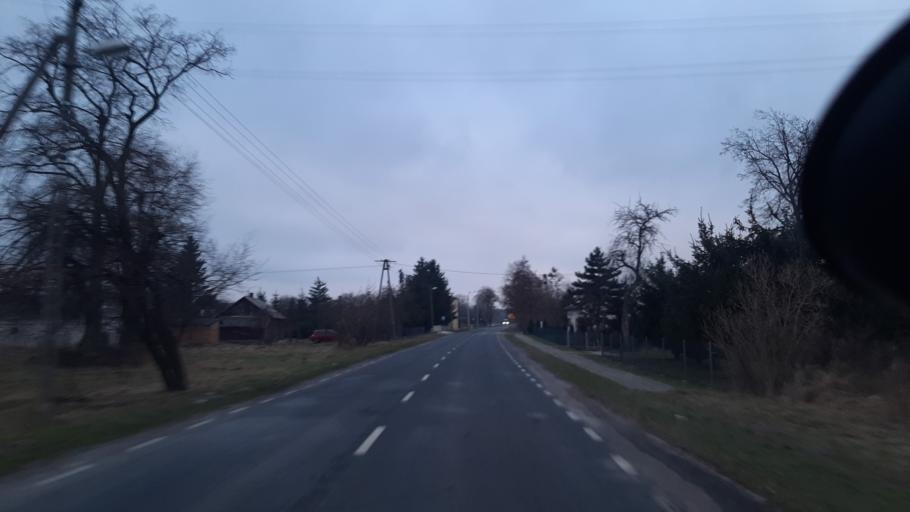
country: PL
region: Lublin Voivodeship
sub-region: Powiat parczewski
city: Debowa Kloda
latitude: 51.6380
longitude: 23.0380
